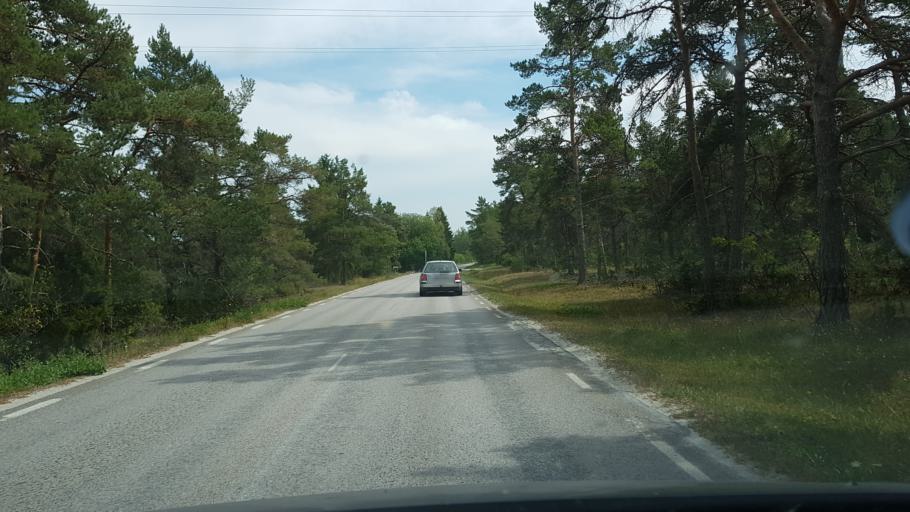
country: SE
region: Gotland
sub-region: Gotland
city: Slite
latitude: 57.7282
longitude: 18.7512
